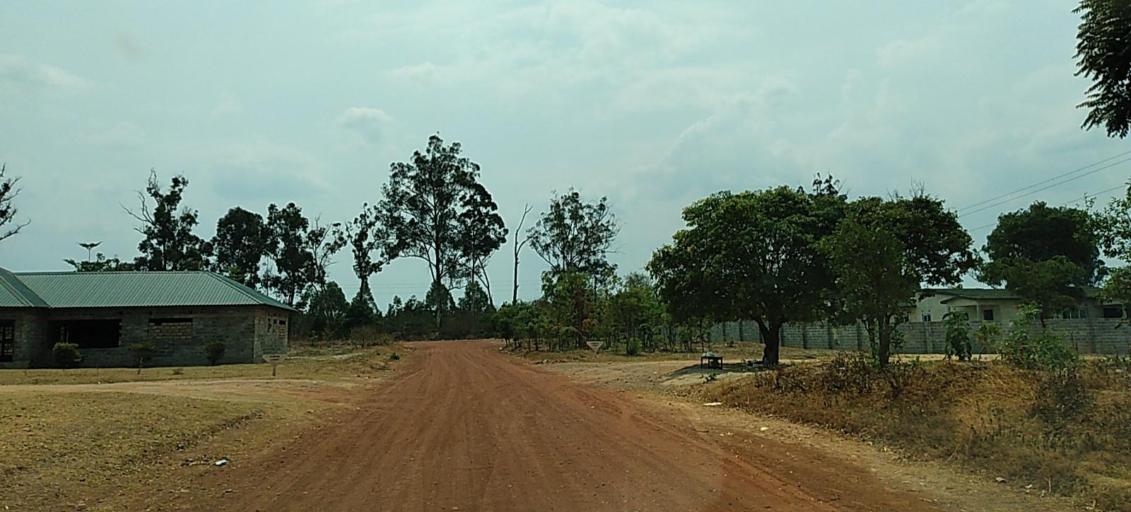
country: ZM
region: Copperbelt
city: Kalulushi
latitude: -12.8324
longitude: 28.0785
